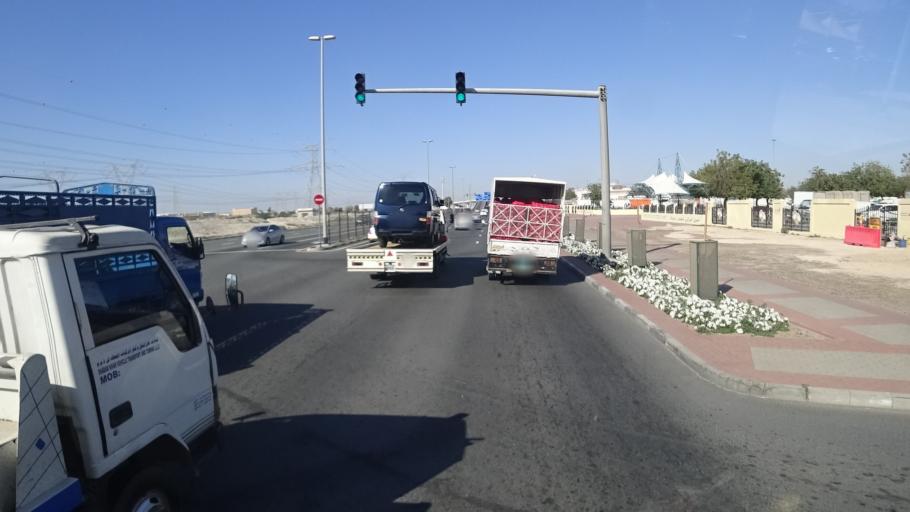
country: AE
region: Ash Shariqah
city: Sharjah
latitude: 25.1765
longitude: 55.3863
